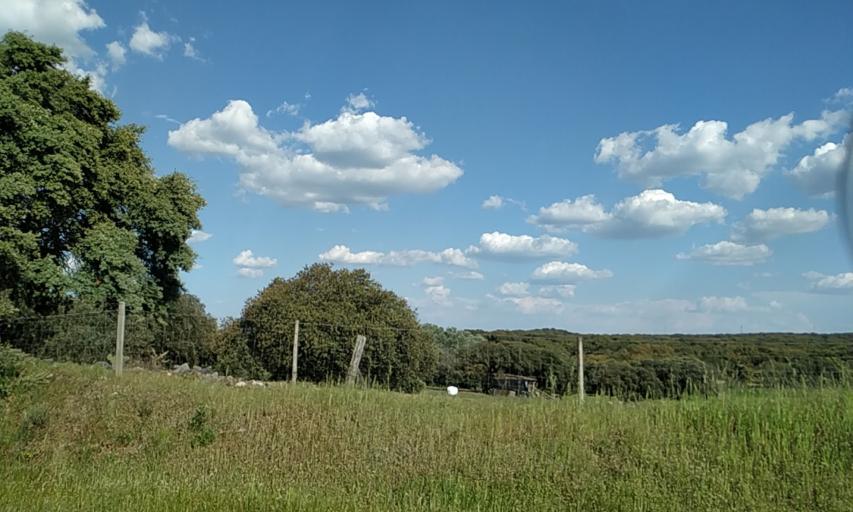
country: PT
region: Evora
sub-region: Estremoz
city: Estremoz
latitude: 38.8711
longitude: -7.5648
